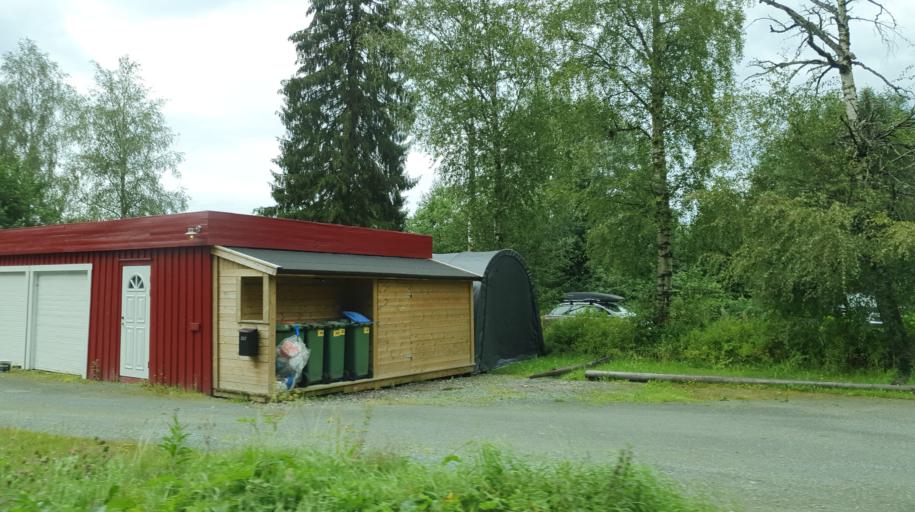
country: NO
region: Nord-Trondelag
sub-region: Stjordal
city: Stjordalshalsen
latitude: 63.4461
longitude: 10.9852
